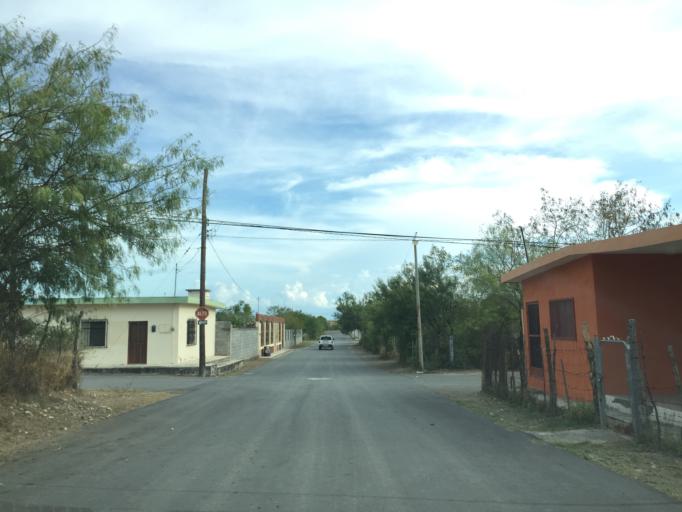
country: MX
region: Nuevo Leon
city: Marin
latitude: 25.8585
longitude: -99.9457
